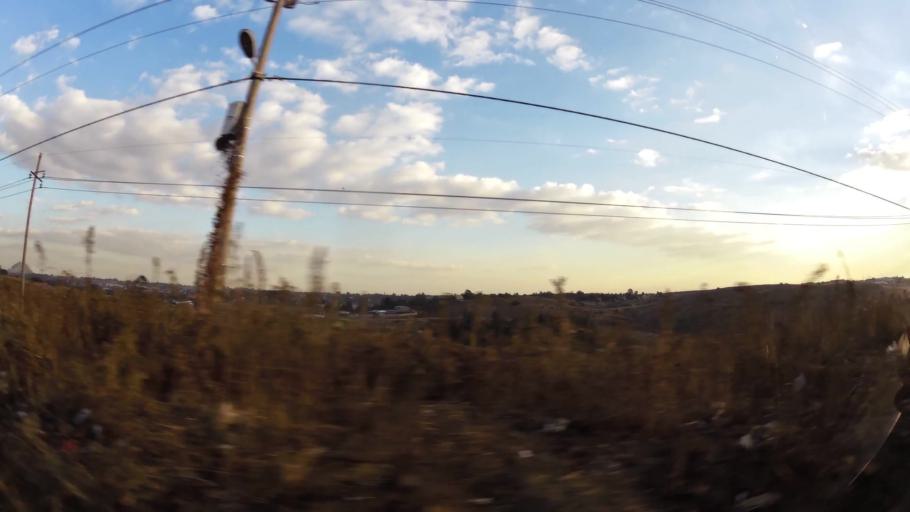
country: ZA
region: Gauteng
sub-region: West Rand District Municipality
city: Krugersdorp
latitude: -26.0804
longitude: 27.7484
